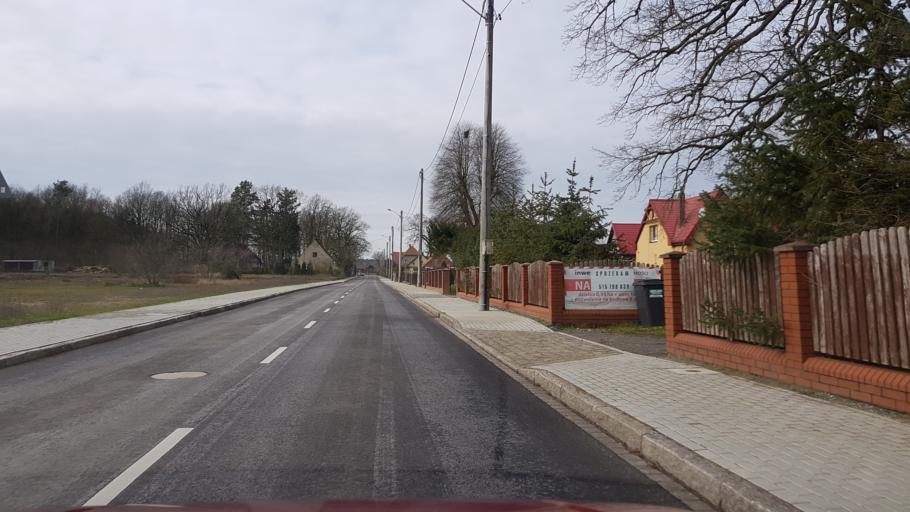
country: PL
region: West Pomeranian Voivodeship
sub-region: Powiat policki
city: Nowe Warpno
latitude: 53.6742
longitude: 14.3869
